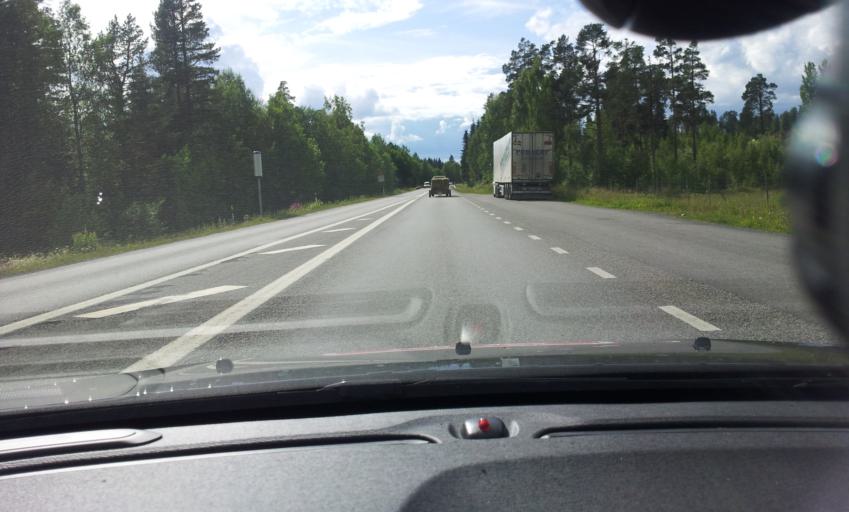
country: SE
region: Jaemtland
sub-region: Are Kommun
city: Jarpen
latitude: 63.3108
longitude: 13.6835
